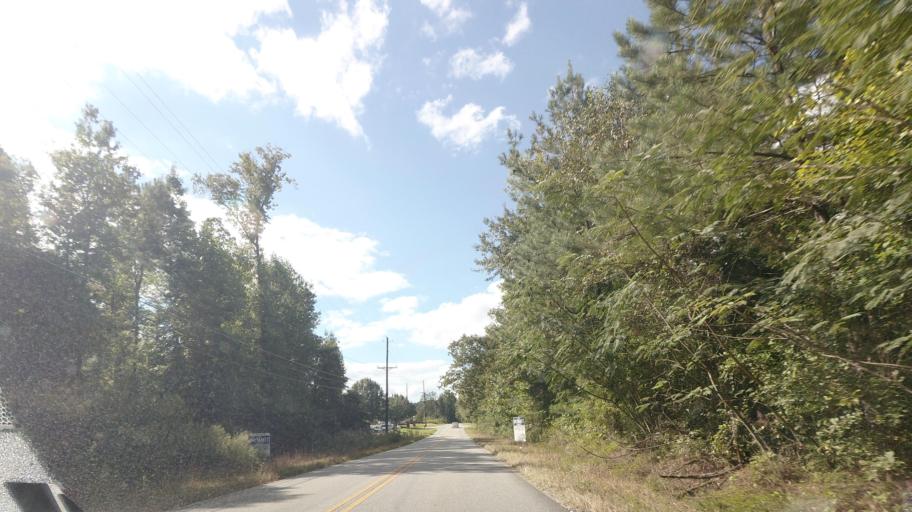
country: US
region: Georgia
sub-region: Bibb County
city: Macon
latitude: 32.9137
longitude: -83.6945
